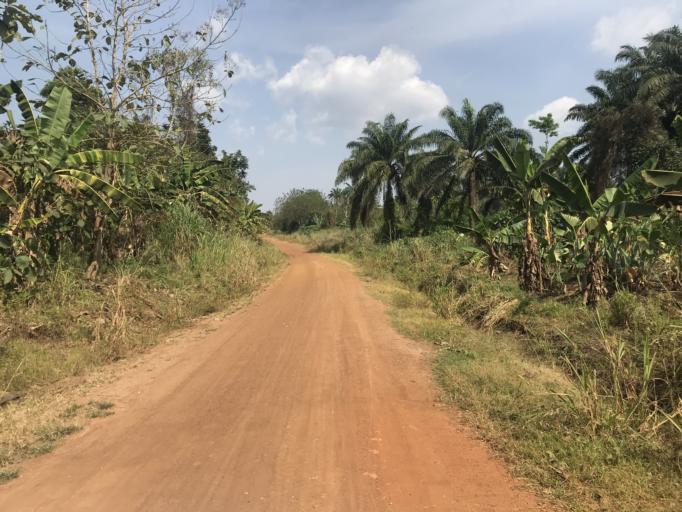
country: NG
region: Osun
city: Osu
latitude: 7.6458
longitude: 4.6572
